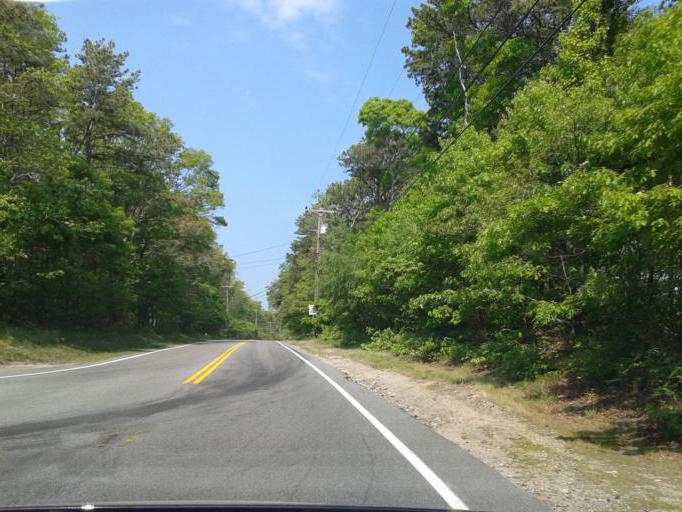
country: US
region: Massachusetts
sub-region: Barnstable County
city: East Falmouth
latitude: 41.6115
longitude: -70.5859
